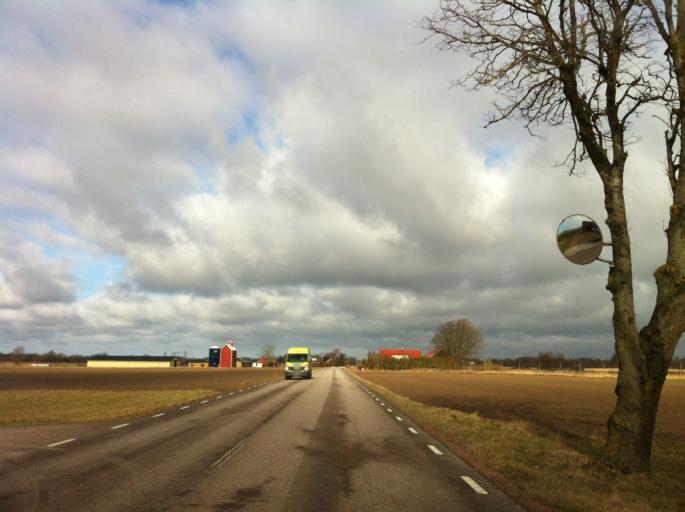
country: SE
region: Skane
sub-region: Helsingborg
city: Hyllinge
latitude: 56.1194
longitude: 12.8877
